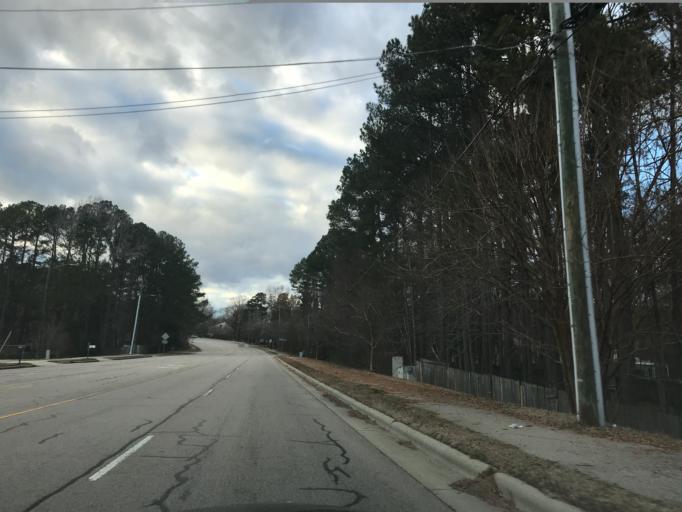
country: US
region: North Carolina
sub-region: Wake County
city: West Raleigh
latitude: 35.8711
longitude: -78.6559
